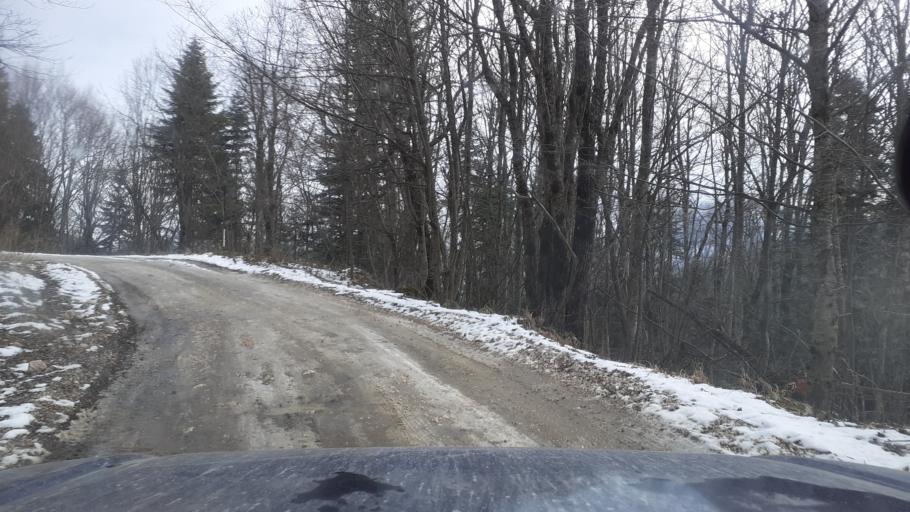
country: RU
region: Krasnodarskiy
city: Neftegorsk
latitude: 44.0726
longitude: 39.7571
